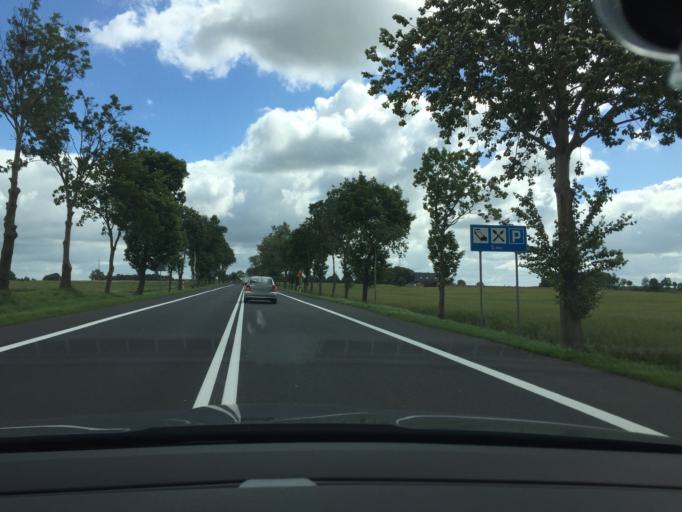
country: PL
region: West Pomeranian Voivodeship
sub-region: Powiat slawienski
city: Slawno
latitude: 54.3381
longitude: 16.6342
